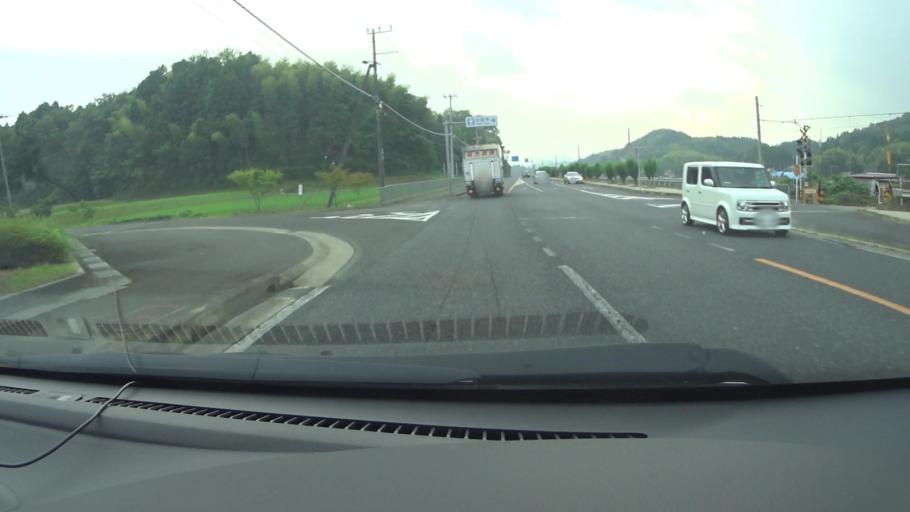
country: JP
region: Kyoto
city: Ayabe
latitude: 35.3377
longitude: 135.3070
